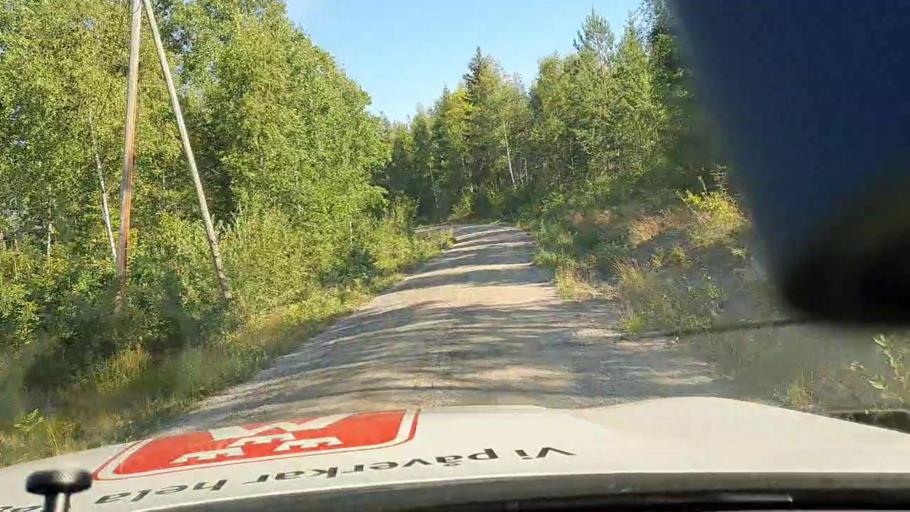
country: SE
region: Soedermanland
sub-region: Eskilstuna Kommun
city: Eskilstuna
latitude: 59.4576
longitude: 16.6502
